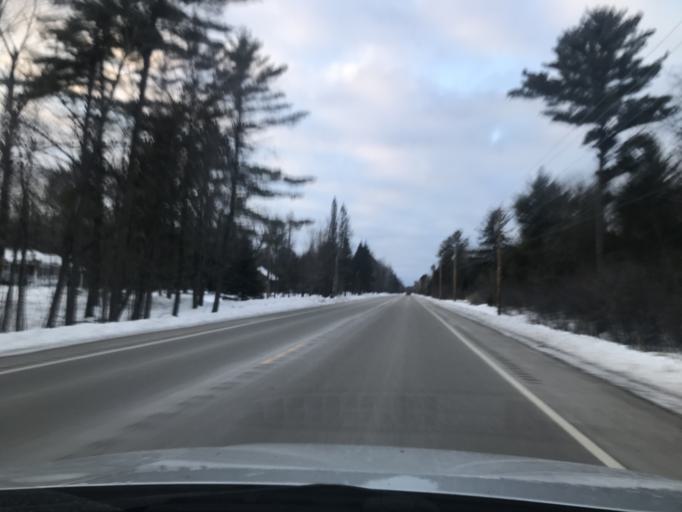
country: US
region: Wisconsin
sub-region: Marinette County
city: Marinette
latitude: 45.1439
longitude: -87.6960
